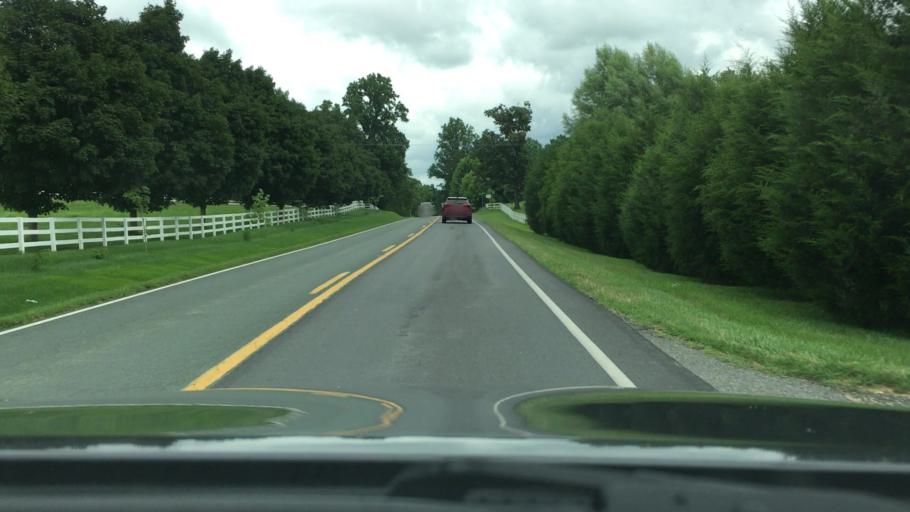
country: US
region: Virginia
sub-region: Orange County
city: Gordonsville
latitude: 38.0795
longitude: -78.2899
